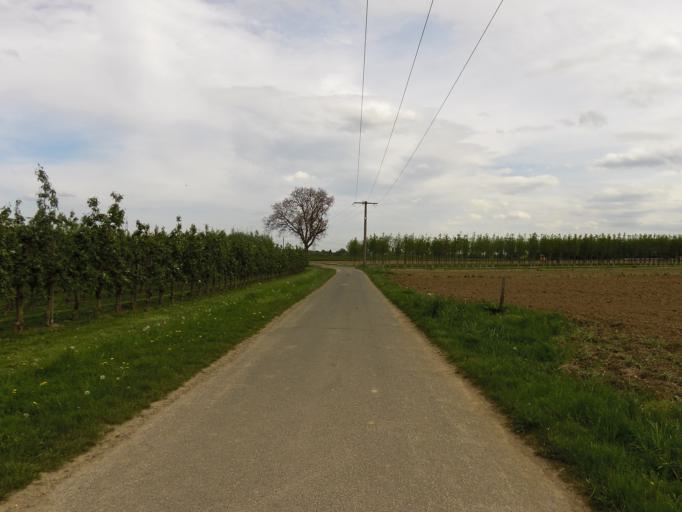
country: DE
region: North Rhine-Westphalia
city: Meckenheim
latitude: 50.6312
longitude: 6.9978
